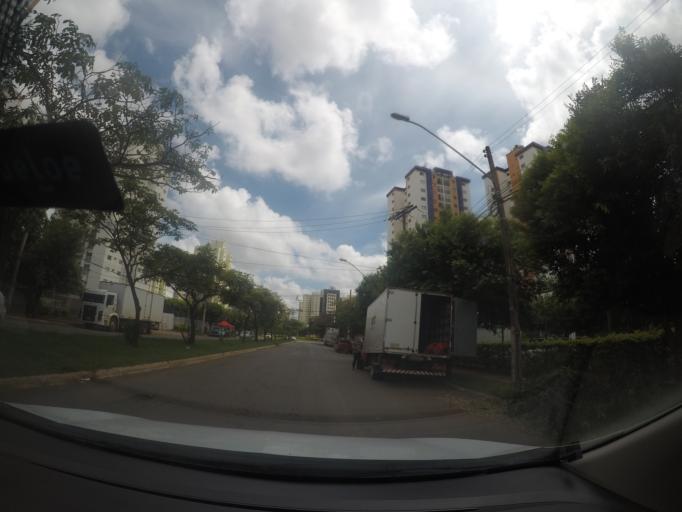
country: BR
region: Goias
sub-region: Goiania
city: Goiania
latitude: -16.7101
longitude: -49.3291
